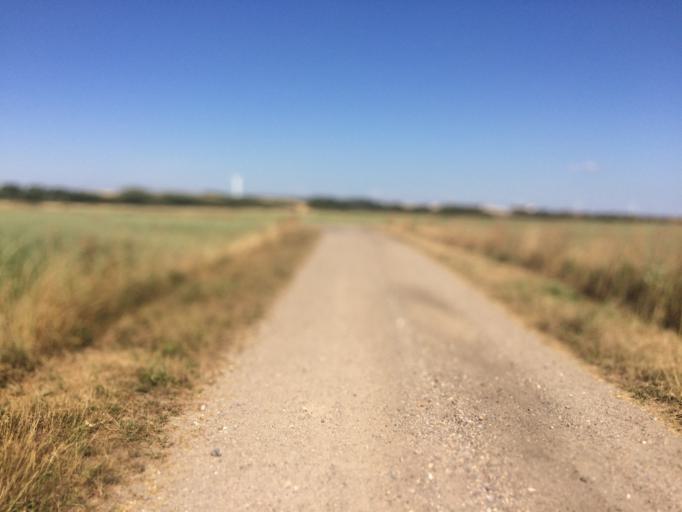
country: DK
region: Central Jutland
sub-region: Holstebro Kommune
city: Vinderup
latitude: 56.5787
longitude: 8.8244
